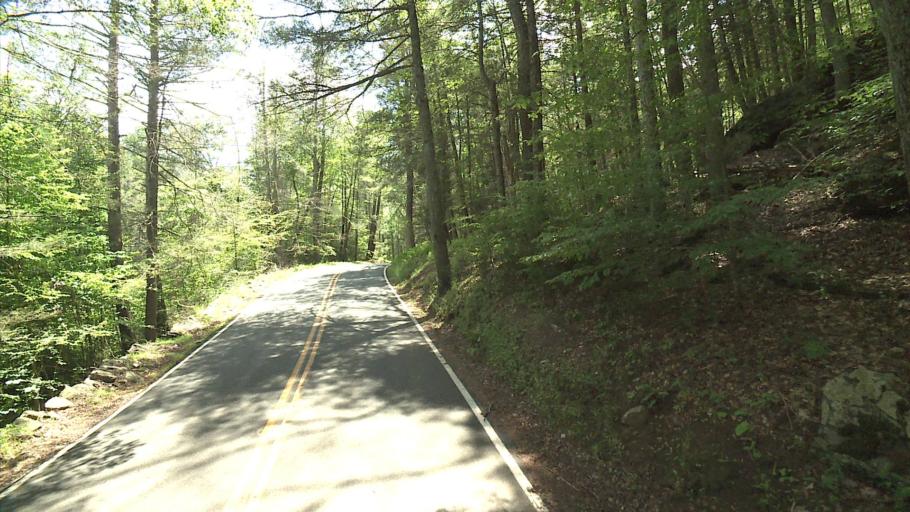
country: US
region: Connecticut
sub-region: New London County
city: Colchester
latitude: 41.4719
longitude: -72.3393
